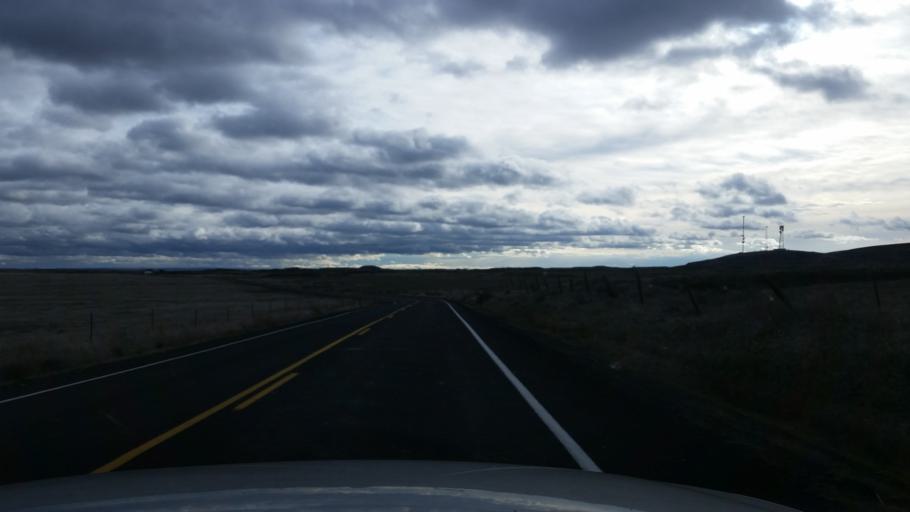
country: US
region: Washington
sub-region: Lincoln County
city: Davenport
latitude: 47.3285
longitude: -117.9833
